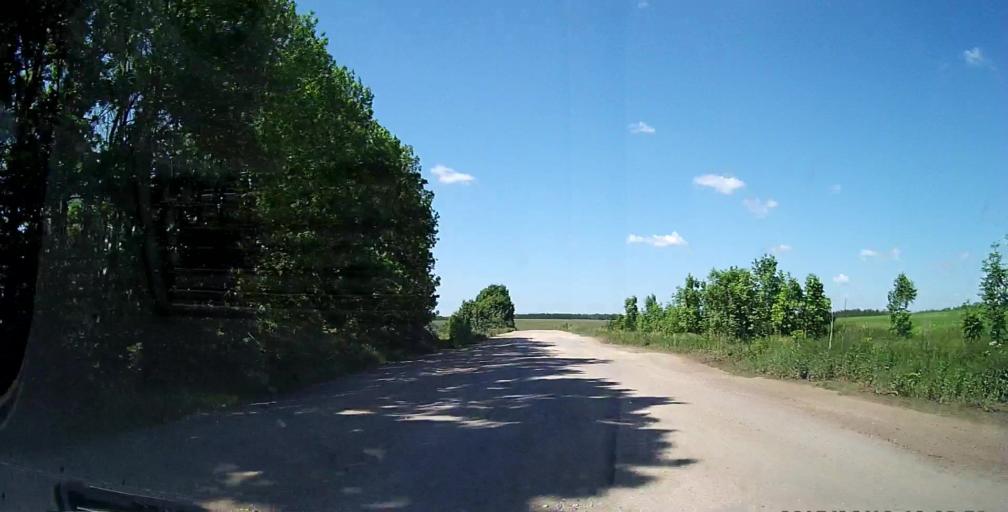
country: RU
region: Tula
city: Kurkino
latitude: 53.2011
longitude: 38.5862
